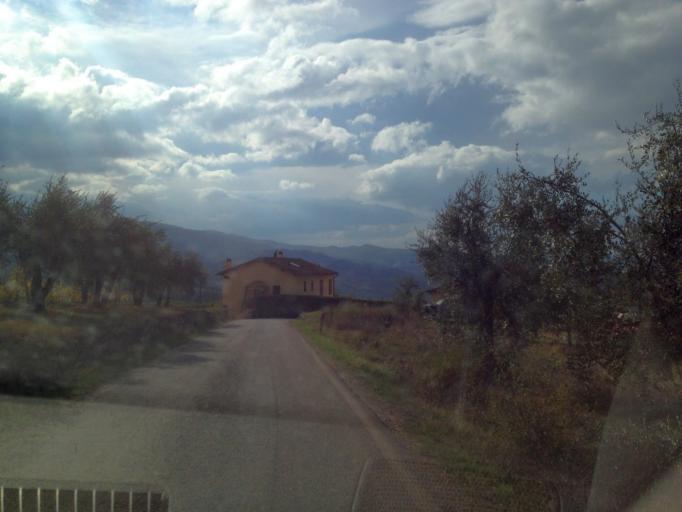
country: IT
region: Tuscany
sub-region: Province of Florence
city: Montebonello
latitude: 43.8559
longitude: 11.5009
